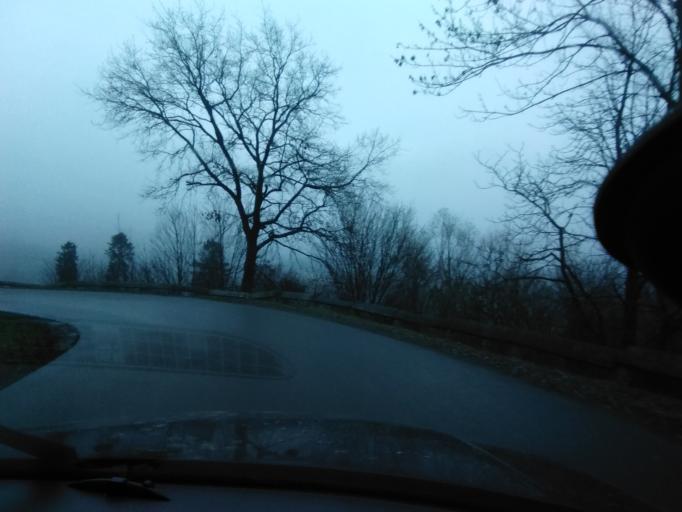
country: PL
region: Subcarpathian Voivodeship
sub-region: Powiat brzozowski
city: Jablonka
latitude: 49.7447
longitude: 22.1118
